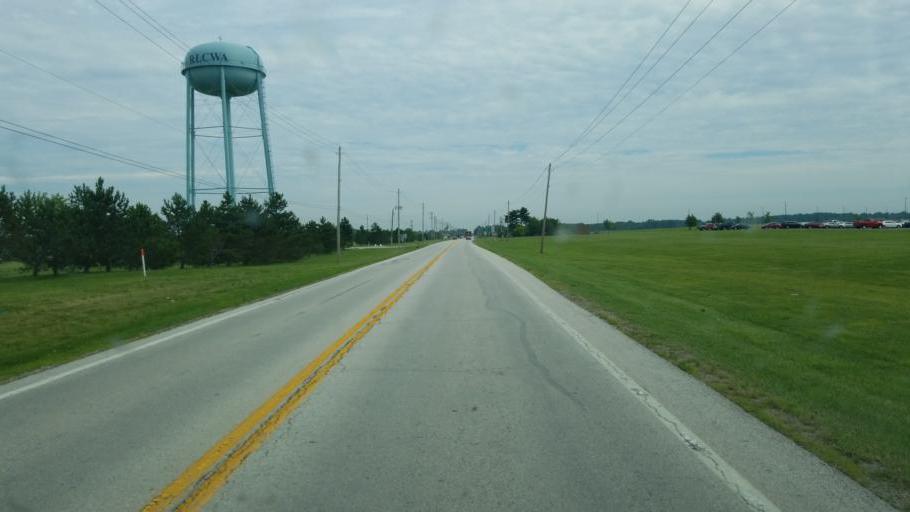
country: US
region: Ohio
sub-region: Lorain County
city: Eaton Estates
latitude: 41.2810
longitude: -82.0210
